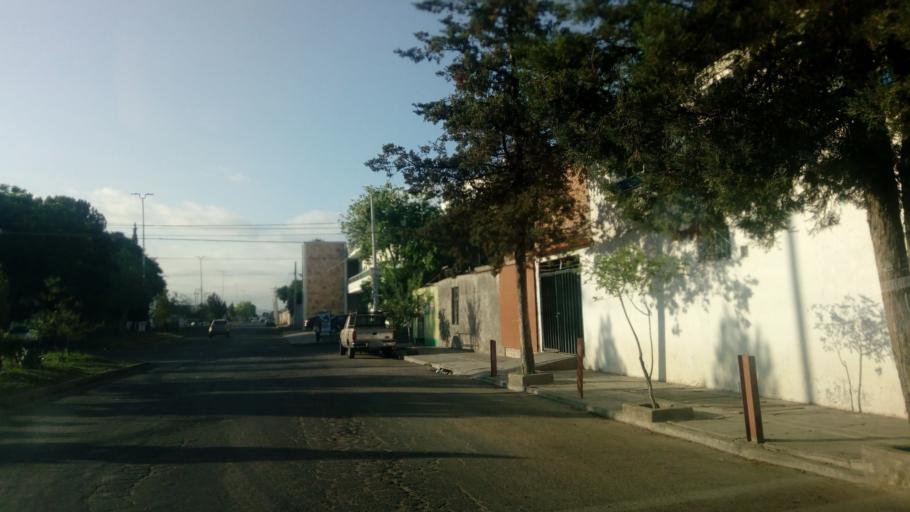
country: MX
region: Durango
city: Victoria de Durango
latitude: 24.0430
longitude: -104.6121
